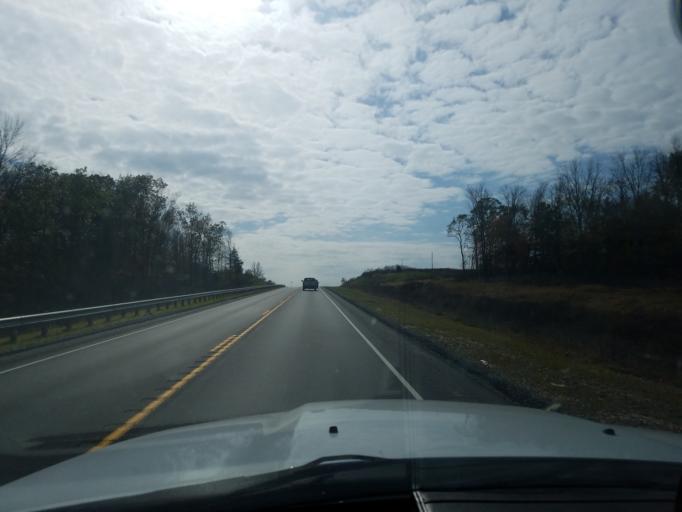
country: US
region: Kentucky
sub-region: Bullitt County
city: Mount Washington
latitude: 37.9824
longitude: -85.4916
